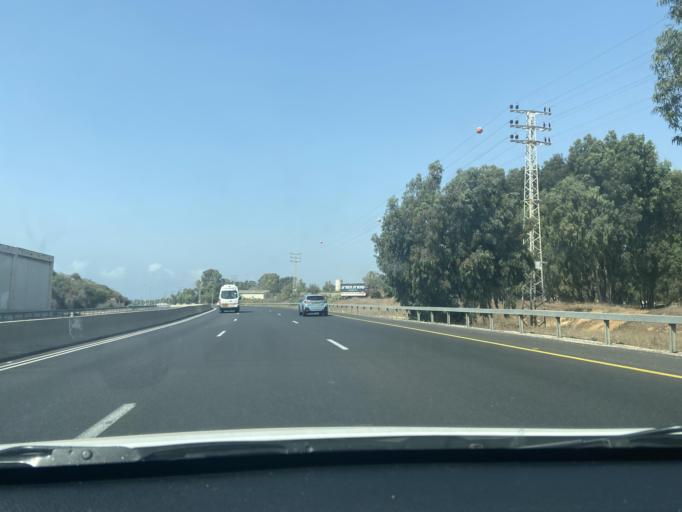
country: IL
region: Northern District
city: `Akko
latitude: 32.9442
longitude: 35.0955
